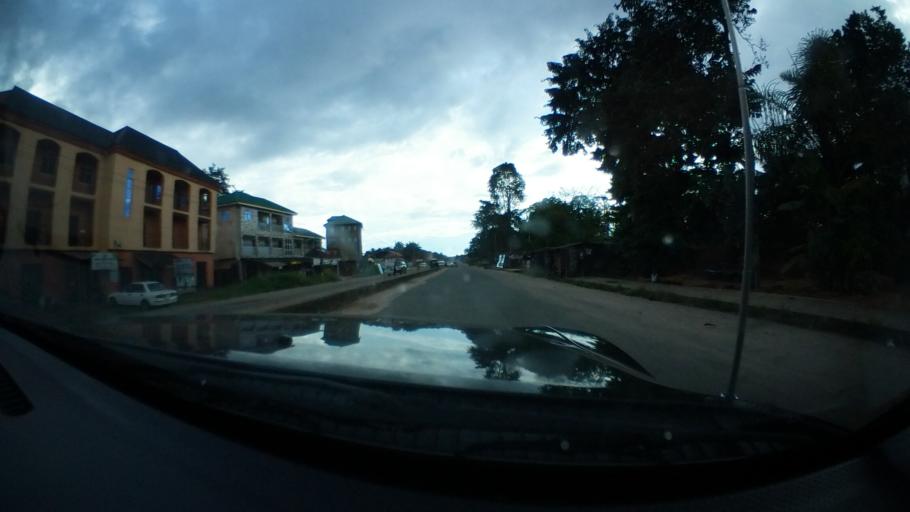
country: NG
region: Imo
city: Orlu
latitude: 5.7963
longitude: 7.0195
